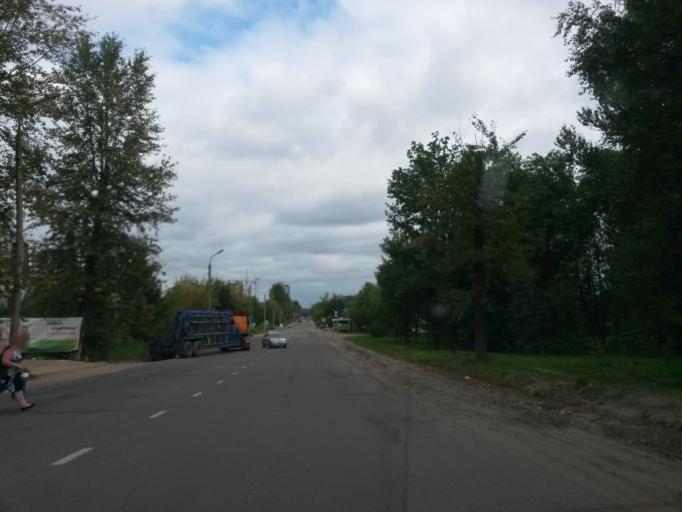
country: RU
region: Jaroslavl
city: Yaroslavl
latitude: 57.5782
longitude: 39.8687
